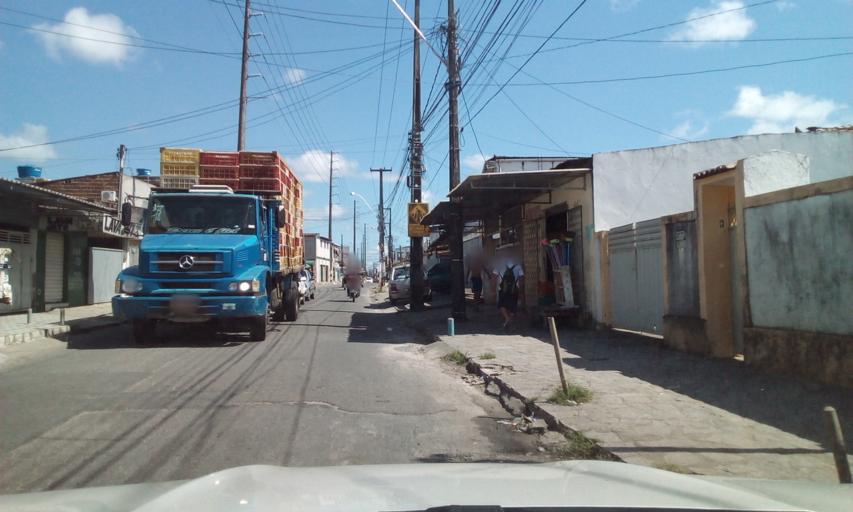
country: BR
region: Paraiba
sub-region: Joao Pessoa
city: Joao Pessoa
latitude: -7.1591
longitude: -34.8784
